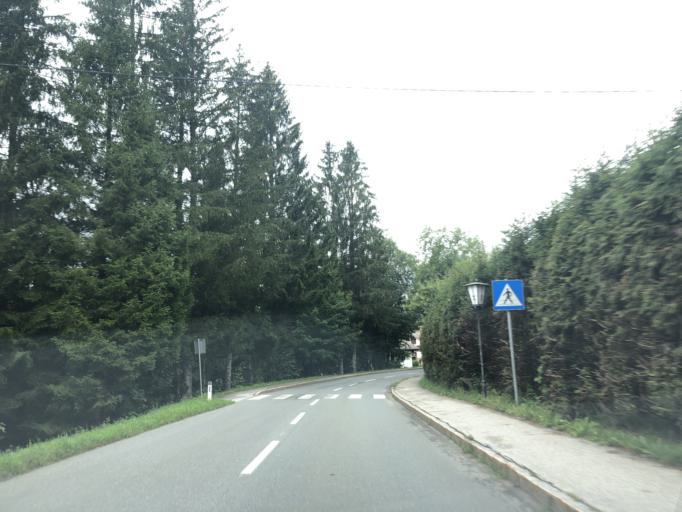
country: AT
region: Tyrol
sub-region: Politischer Bezirk Kufstein
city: Scheffau am Wilden Kaiser
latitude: 47.5301
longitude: 12.2464
